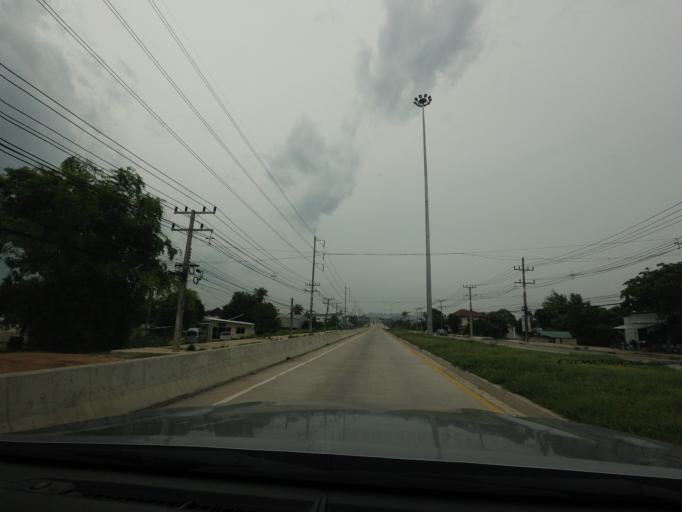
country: TH
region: Songkhla
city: Songkhla
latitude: 7.1278
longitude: 100.5832
